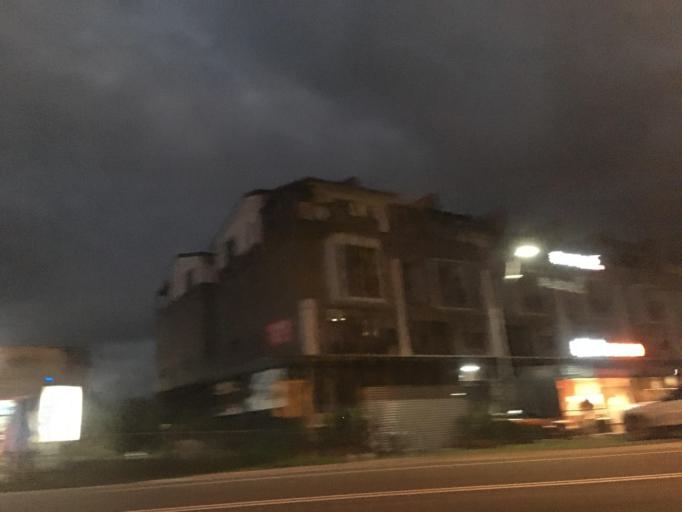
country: TW
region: Taiwan
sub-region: Yilan
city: Yilan
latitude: 24.8630
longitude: 121.8286
